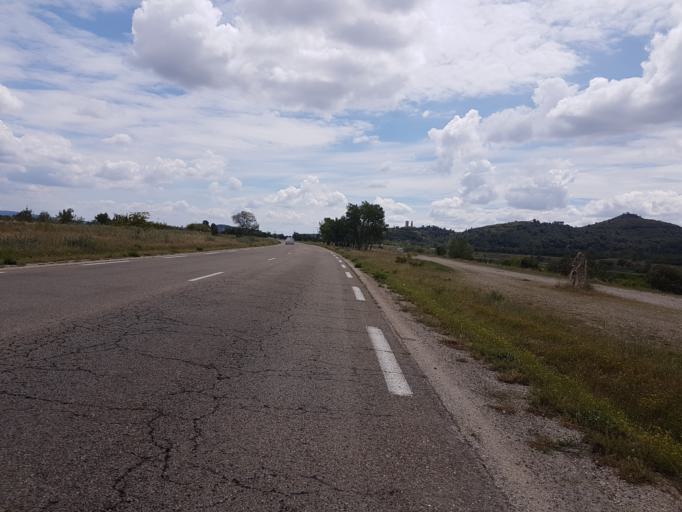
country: FR
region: Languedoc-Roussillon
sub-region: Departement du Gard
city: Vallabregues
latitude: 43.8532
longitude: 4.6175
